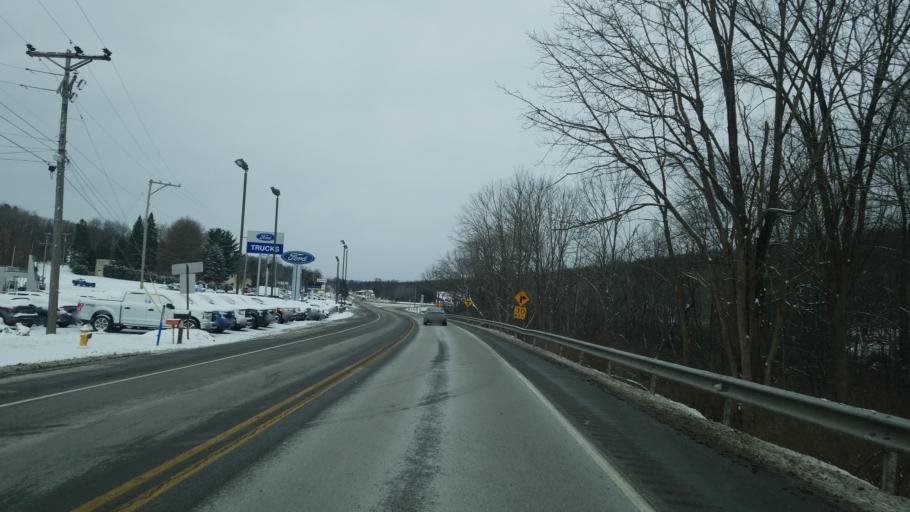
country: US
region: Pennsylvania
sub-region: Clearfield County
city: Sandy
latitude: 41.0900
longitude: -78.7736
